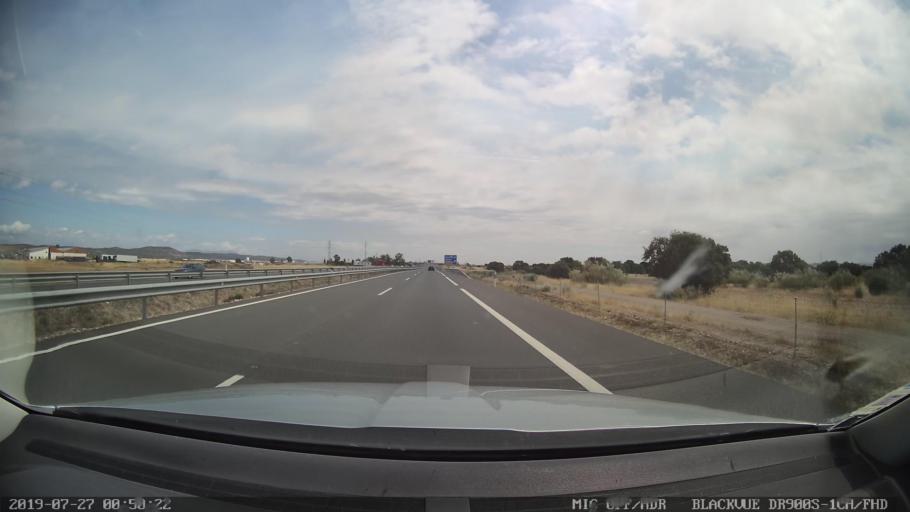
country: ES
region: Castille-La Mancha
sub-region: Province of Toledo
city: Velada
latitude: 39.9391
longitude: -4.9622
